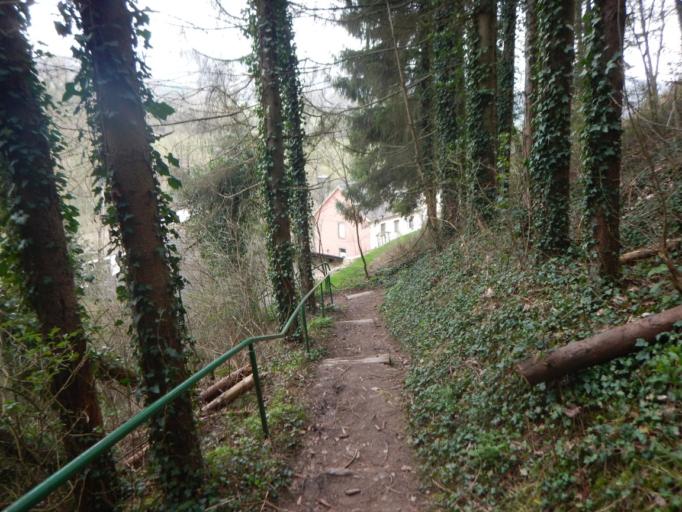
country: LU
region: Grevenmacher
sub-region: Canton d'Echternach
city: Berdorf
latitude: 49.8355
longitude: 6.3285
